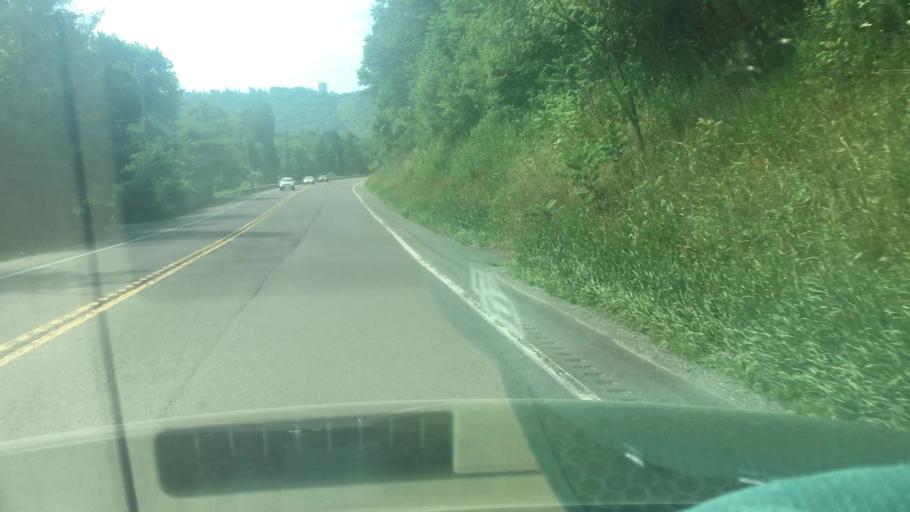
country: US
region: Pennsylvania
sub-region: Northumberland County
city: Kulpmont
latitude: 40.8303
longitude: -76.5043
